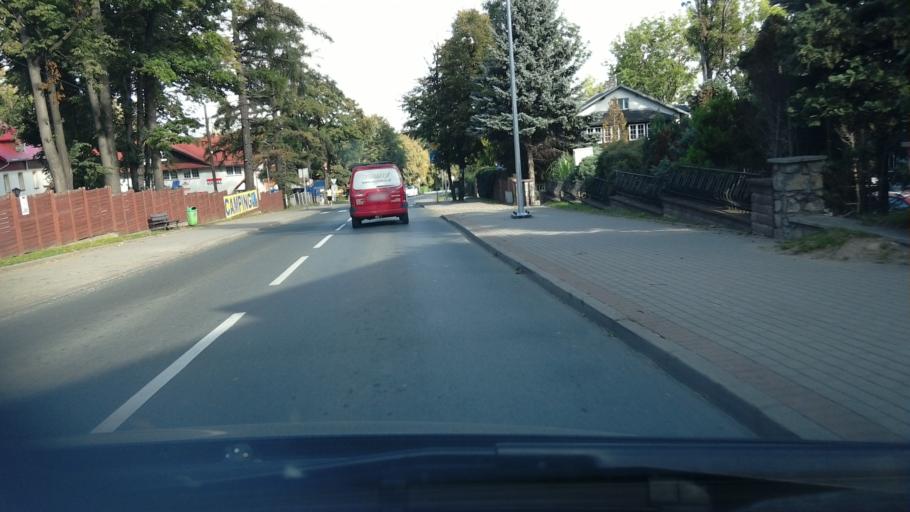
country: PL
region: Lower Silesian Voivodeship
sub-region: Powiat jeleniogorski
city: Karpacz
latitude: 50.7802
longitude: 15.7629
